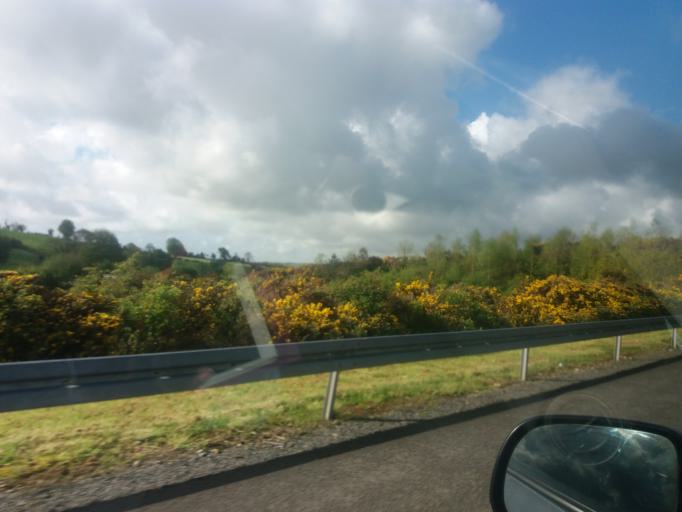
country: IE
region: Leinster
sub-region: Loch Garman
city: Gorey
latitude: 52.6500
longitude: -6.3176
